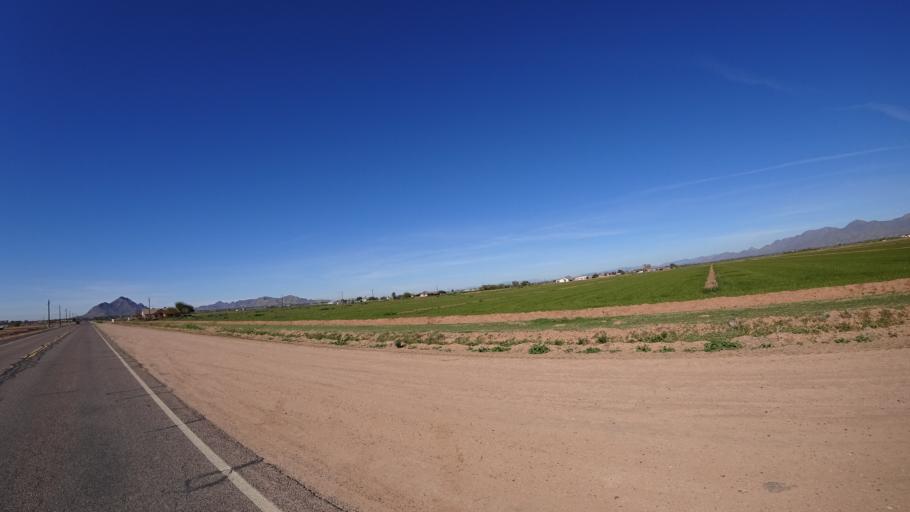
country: US
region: Arizona
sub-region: Maricopa County
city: Scottsdale
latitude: 33.5096
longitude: -111.8629
